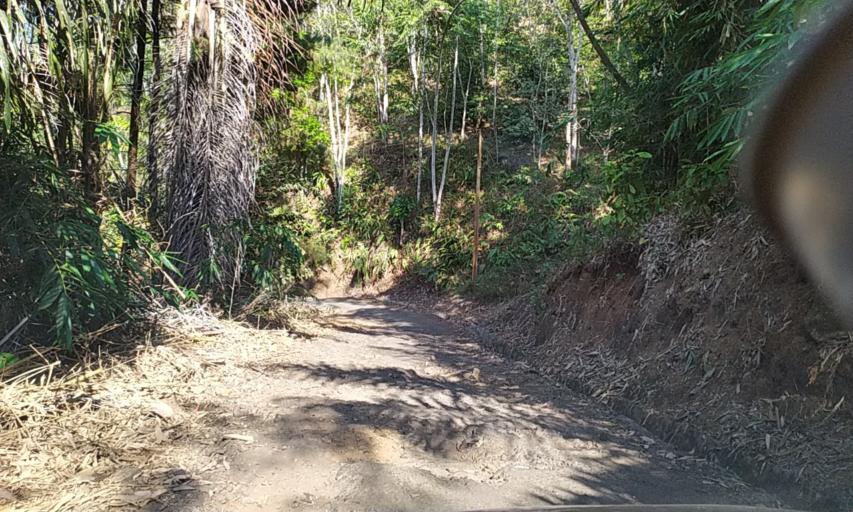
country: ID
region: Central Java
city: Datar
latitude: -7.2166
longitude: 108.6235
